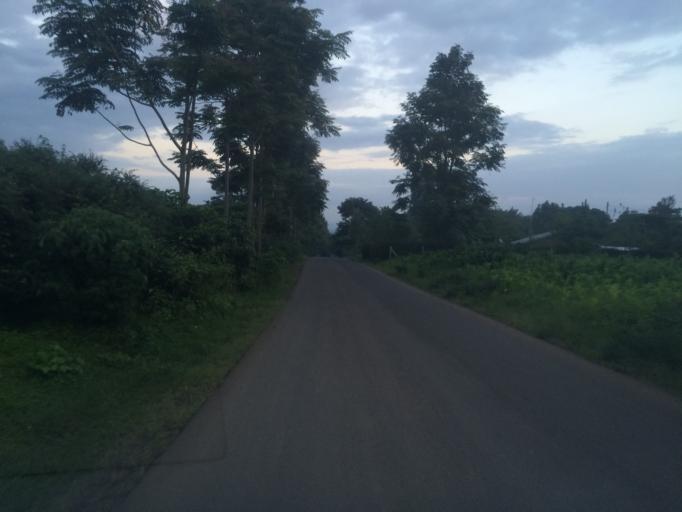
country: TZ
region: Arusha
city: Nkoaranga
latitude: -3.3600
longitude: 36.8146
